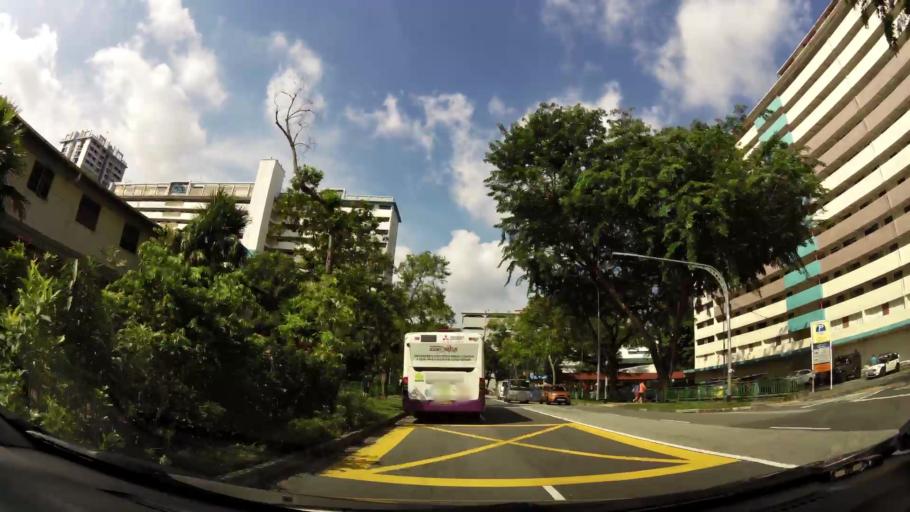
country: SG
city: Singapore
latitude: 1.3181
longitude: 103.8790
